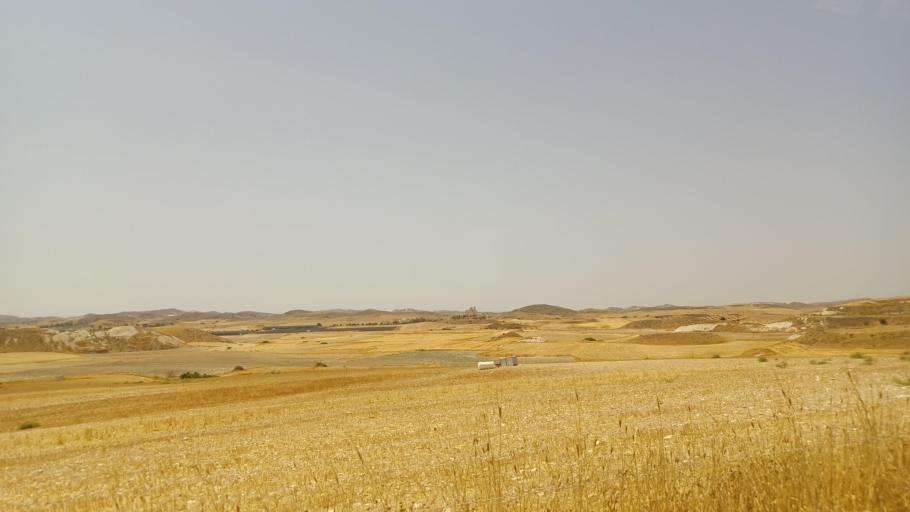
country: CY
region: Larnaka
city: Troulloi
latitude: 35.0377
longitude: 33.5945
